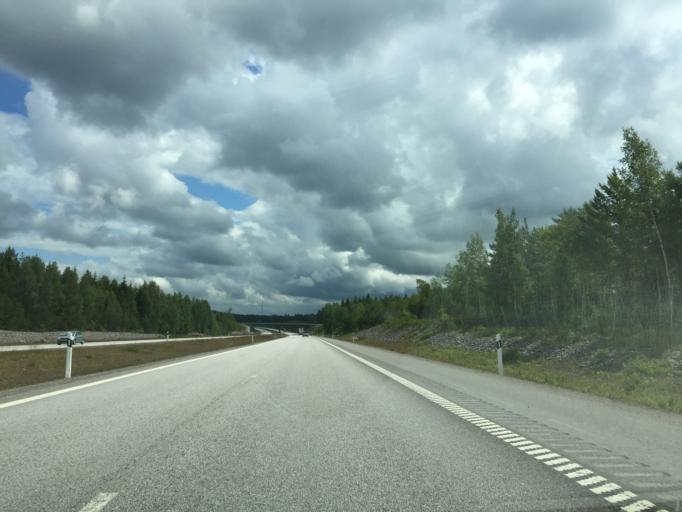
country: SE
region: OErebro
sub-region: Lindesbergs Kommun
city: Fellingsbro
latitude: 59.3764
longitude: 15.6180
